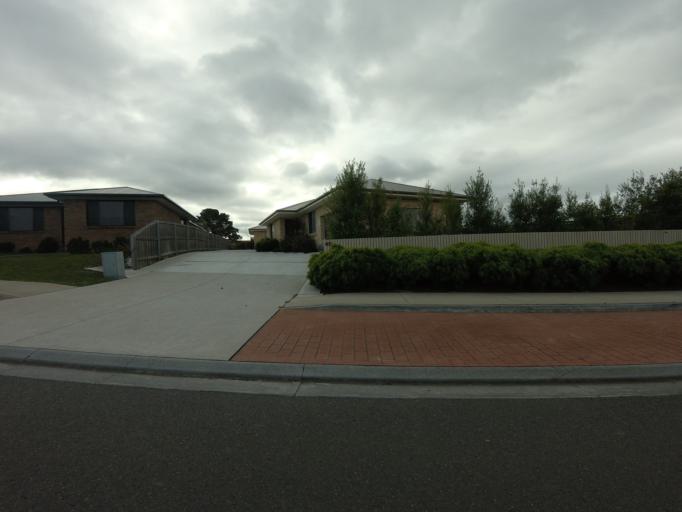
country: AU
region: Tasmania
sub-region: Clarence
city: Howrah
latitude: -42.8868
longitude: 147.4239
